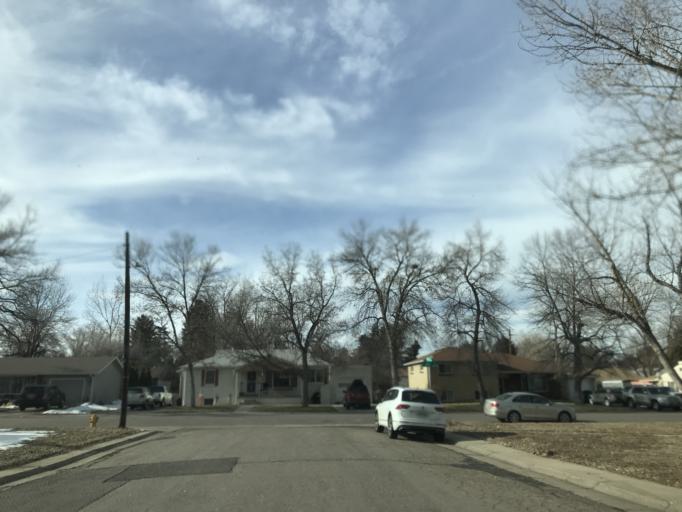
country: US
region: Colorado
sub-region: Arapahoe County
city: Littleton
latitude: 39.6030
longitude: -105.0135
